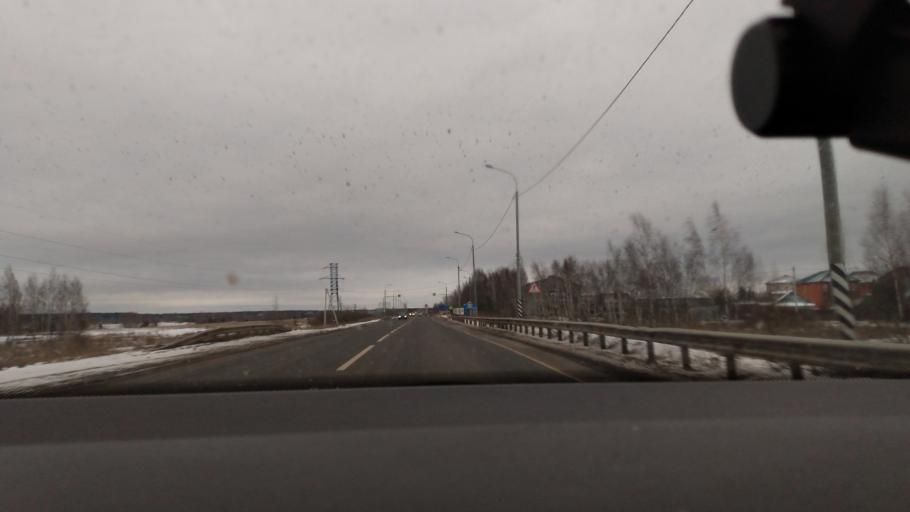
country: RU
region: Moskovskaya
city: Yegor'yevsk
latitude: 55.3943
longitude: 39.0696
